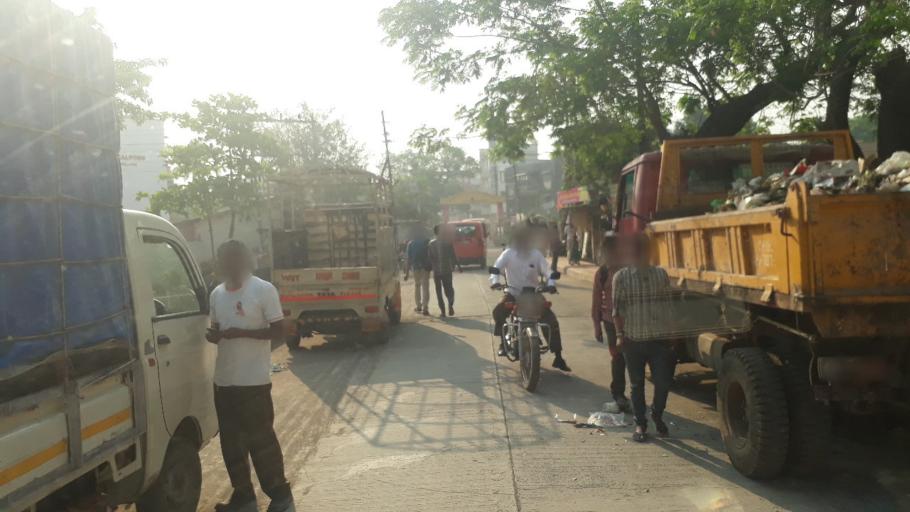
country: IN
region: Maharashtra
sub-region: Raigarh
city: Neral
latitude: 19.0235
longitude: 73.3169
